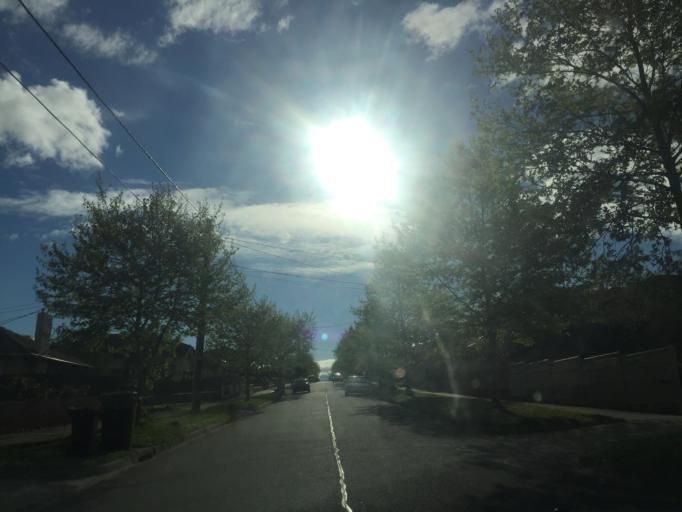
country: AU
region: Victoria
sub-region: Darebin
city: Preston
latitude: -37.7312
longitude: 145.0235
